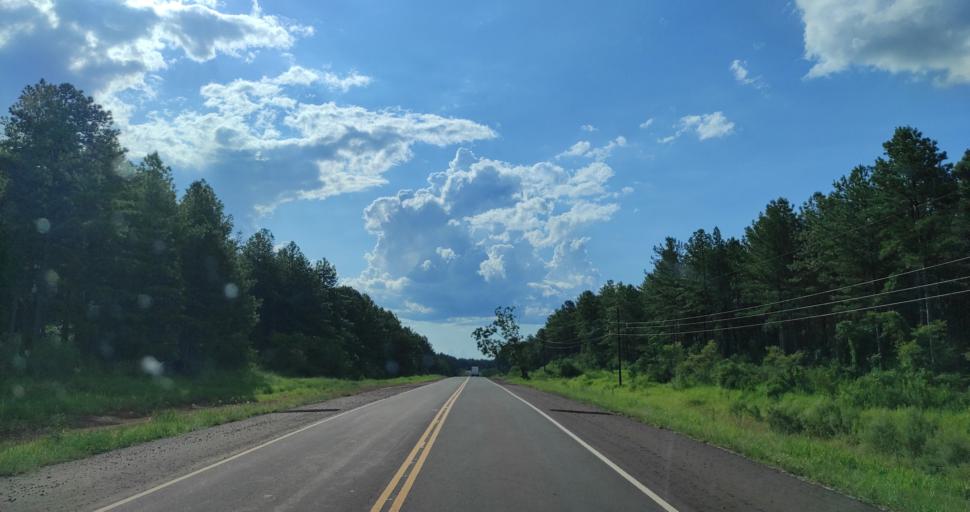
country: AR
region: Misiones
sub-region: Departamento de San Pedro
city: San Pedro
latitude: -26.3524
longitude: -53.9620
